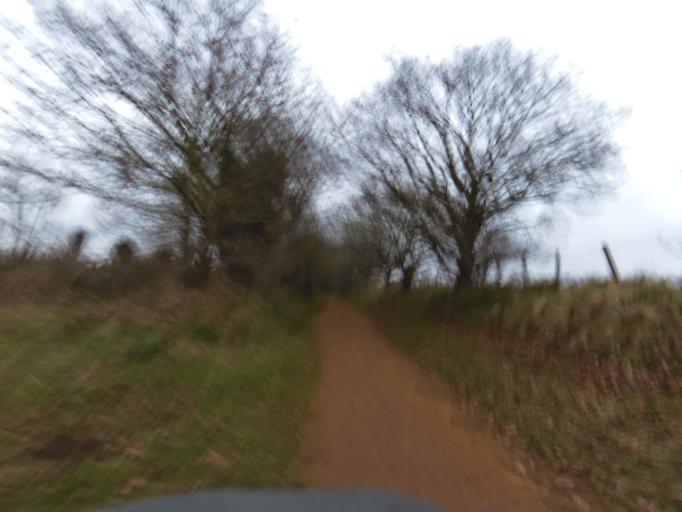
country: GB
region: England
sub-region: Norfolk
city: Costessey
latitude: 52.6917
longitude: 1.2053
